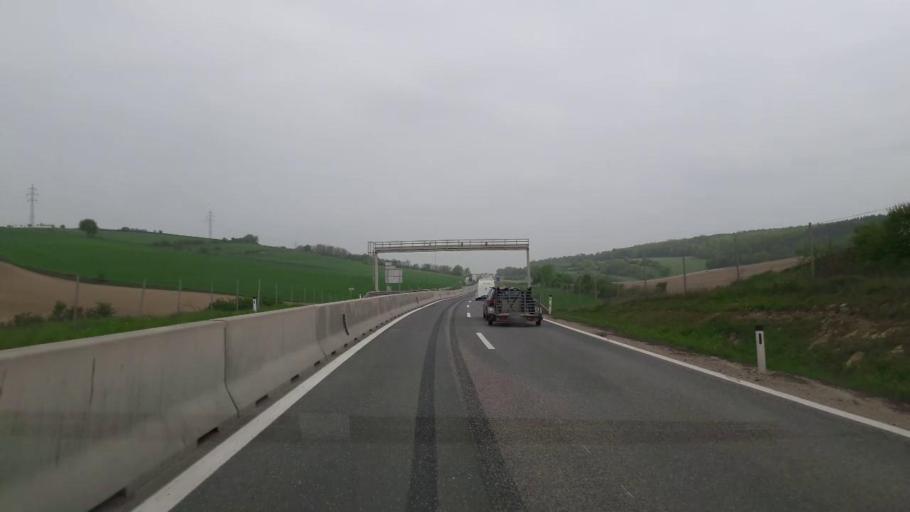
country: AT
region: Lower Austria
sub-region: Politischer Bezirk Hollabrunn
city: Hollabrunn
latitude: 48.5139
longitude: 16.0881
